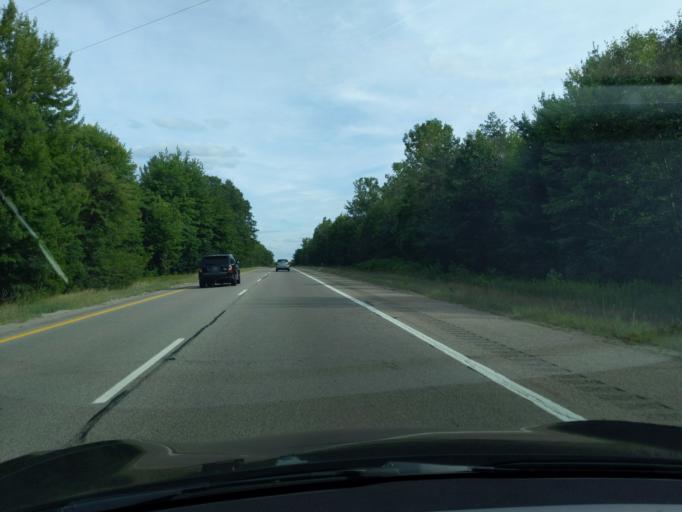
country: US
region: Michigan
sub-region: Muskegon County
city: Fruitport
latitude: 43.1107
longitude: -86.1219
